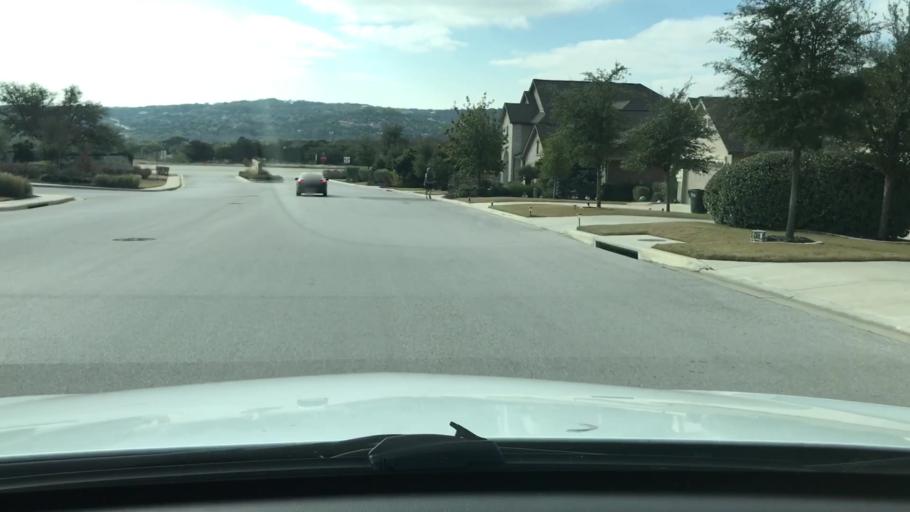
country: US
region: Texas
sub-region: Travis County
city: Bee Cave
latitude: 30.3142
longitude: -97.9605
